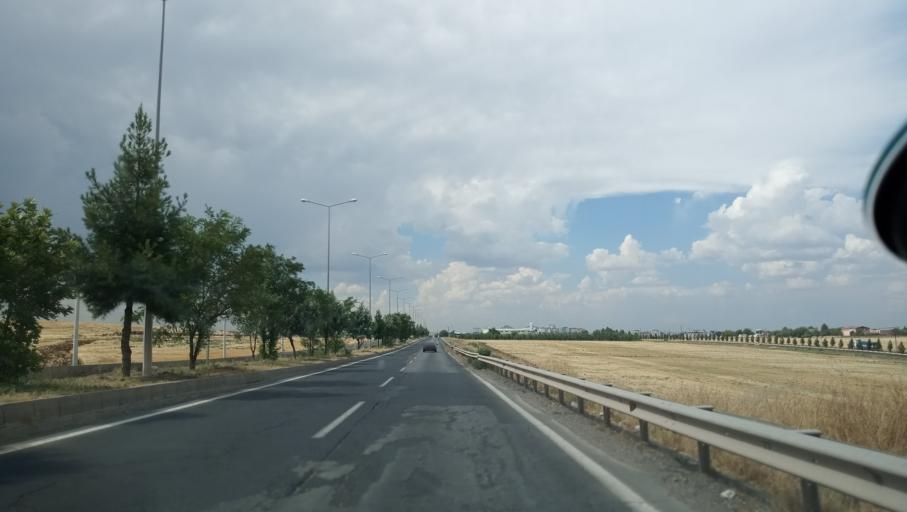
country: TR
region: Diyarbakir
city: Diyarbakir
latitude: 37.8761
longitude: 40.2208
